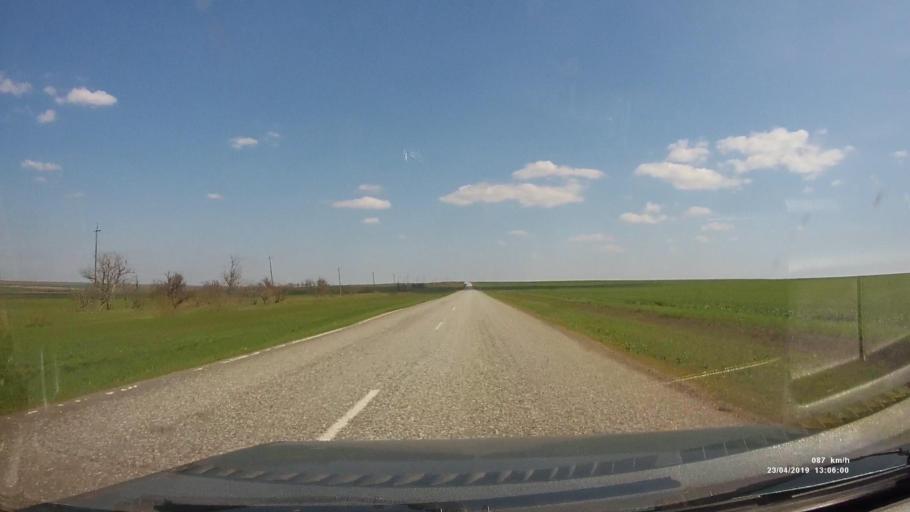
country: RU
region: Kalmykiya
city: Yashalta
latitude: 46.5918
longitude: 42.7325
